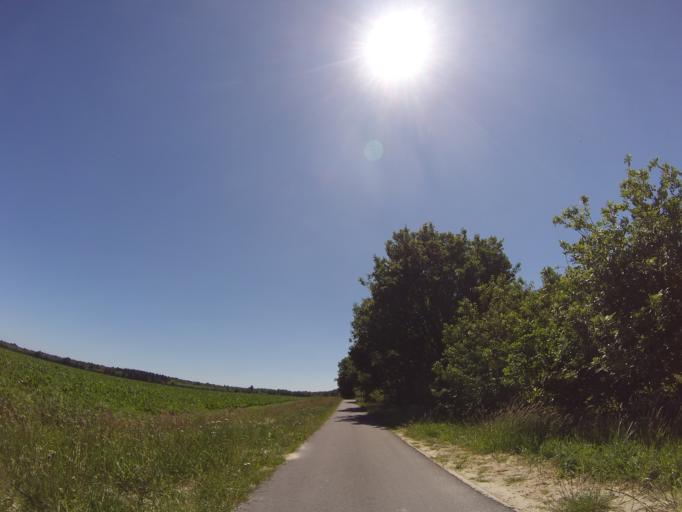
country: NL
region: Drenthe
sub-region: Gemeente Assen
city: Assen
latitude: 52.9362
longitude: 6.5719
